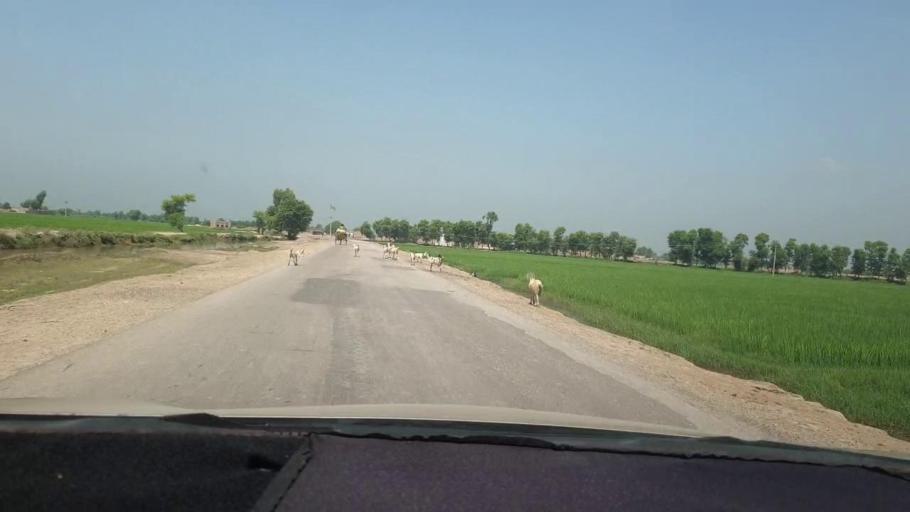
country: PK
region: Sindh
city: Miro Khan
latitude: 27.7699
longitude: 68.0651
